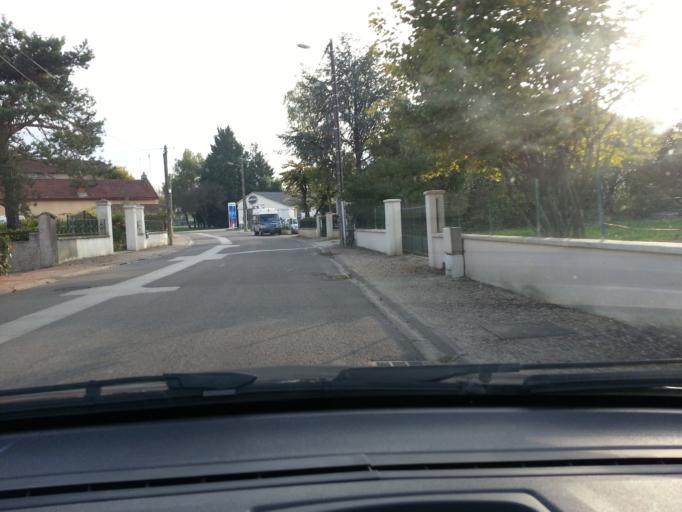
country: FR
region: Bourgogne
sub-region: Departement de Saone-et-Loire
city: Saint-Remy
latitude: 46.7755
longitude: 4.8211
